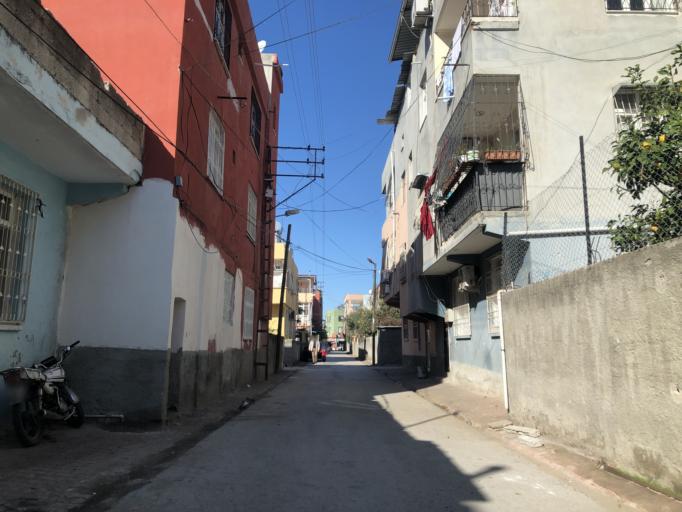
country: TR
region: Adana
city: Yuregir
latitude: 37.0075
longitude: 35.3660
